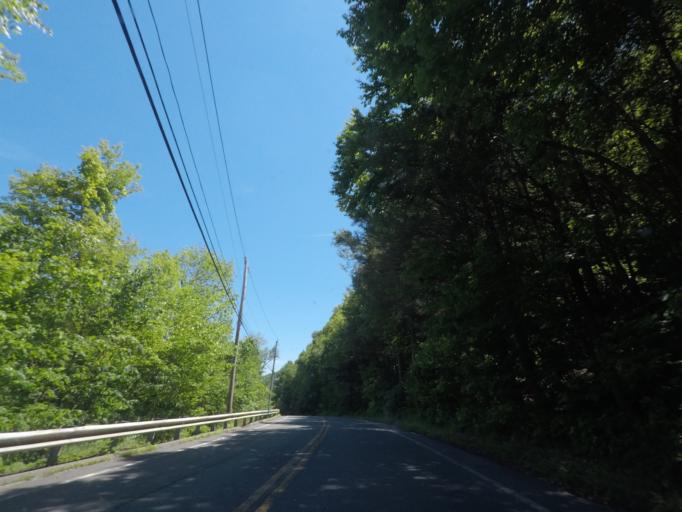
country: US
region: Massachusetts
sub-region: Berkshire County
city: Becket
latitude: 42.2627
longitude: -72.9625
